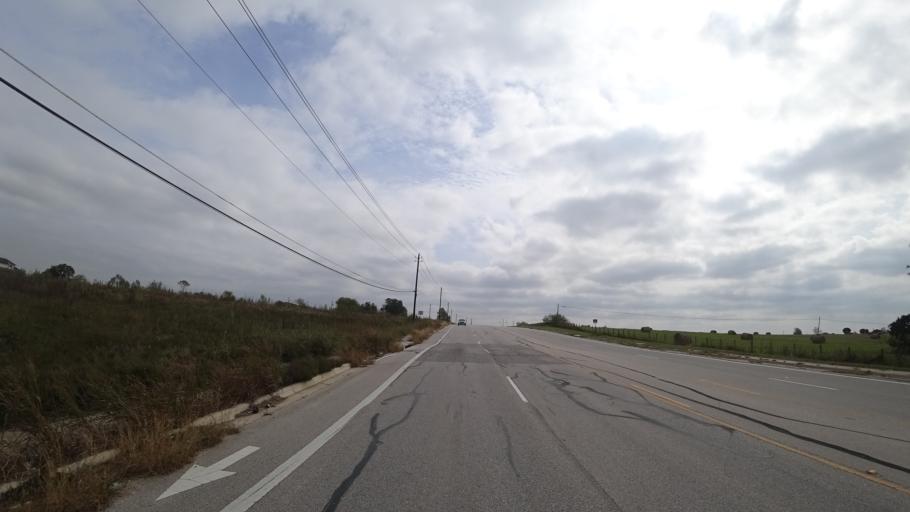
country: US
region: Texas
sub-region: Travis County
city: Pflugerville
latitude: 30.3872
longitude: -97.6179
